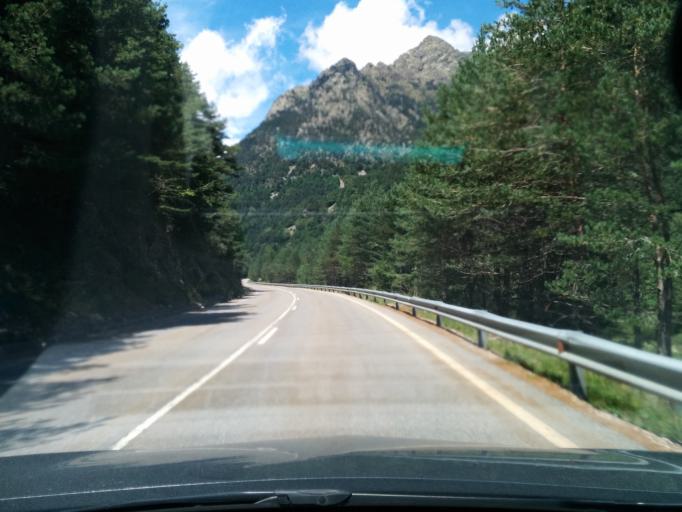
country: ES
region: Aragon
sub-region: Provincia de Huesca
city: Bielsa
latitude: 42.6808
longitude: 0.2133
